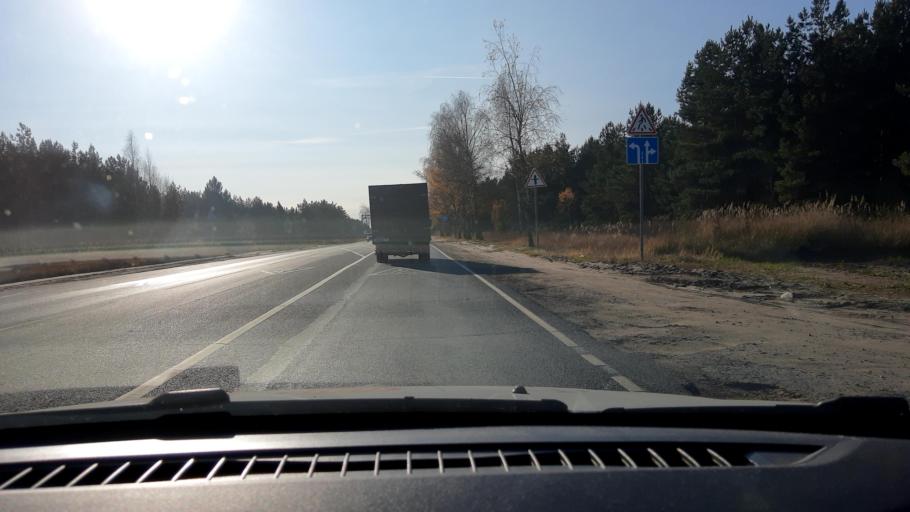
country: RU
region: Nizjnij Novgorod
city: Dzerzhinsk
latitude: 56.2905
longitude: 43.4758
